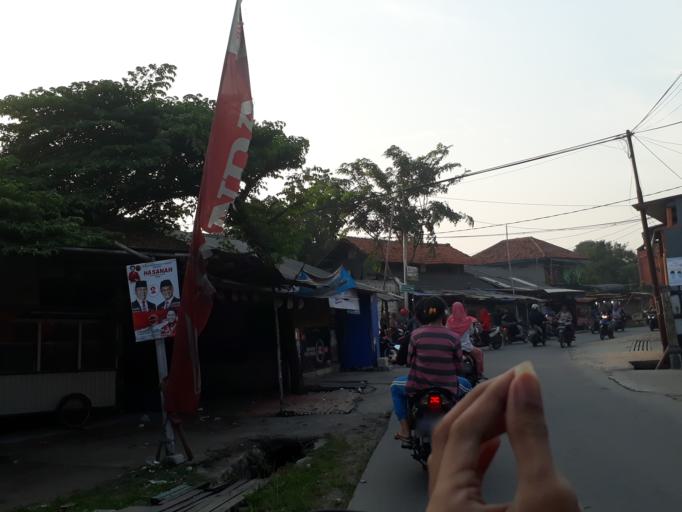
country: ID
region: West Java
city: Bekasi
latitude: -6.2442
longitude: 107.0569
